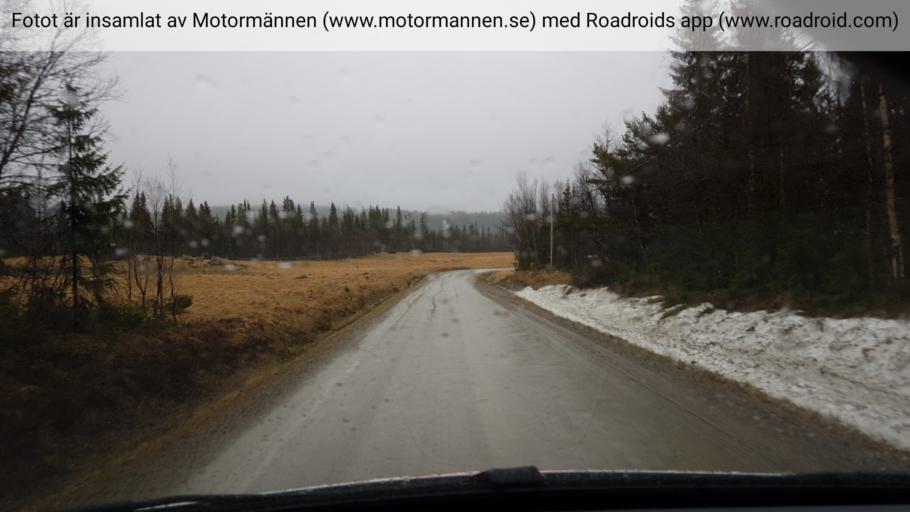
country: SE
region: Jaemtland
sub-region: Are Kommun
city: Jarpen
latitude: 62.5981
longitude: 13.2428
